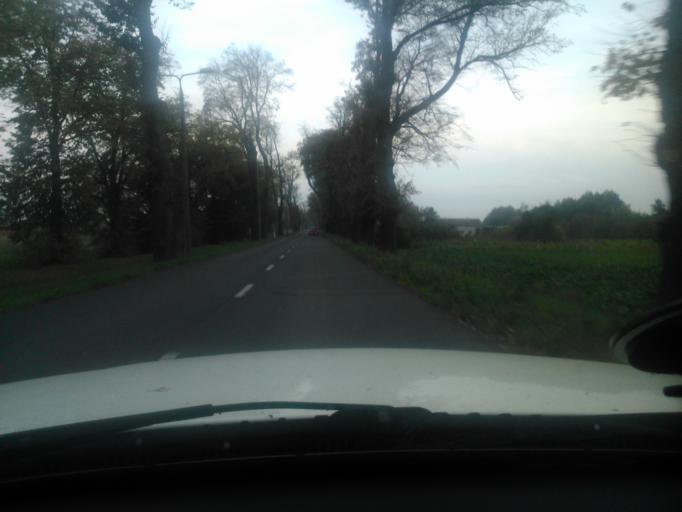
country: PL
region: Kujawsko-Pomorskie
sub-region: Powiat golubsko-dobrzynski
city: Kowalewo Pomorskie
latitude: 53.1587
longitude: 18.8845
